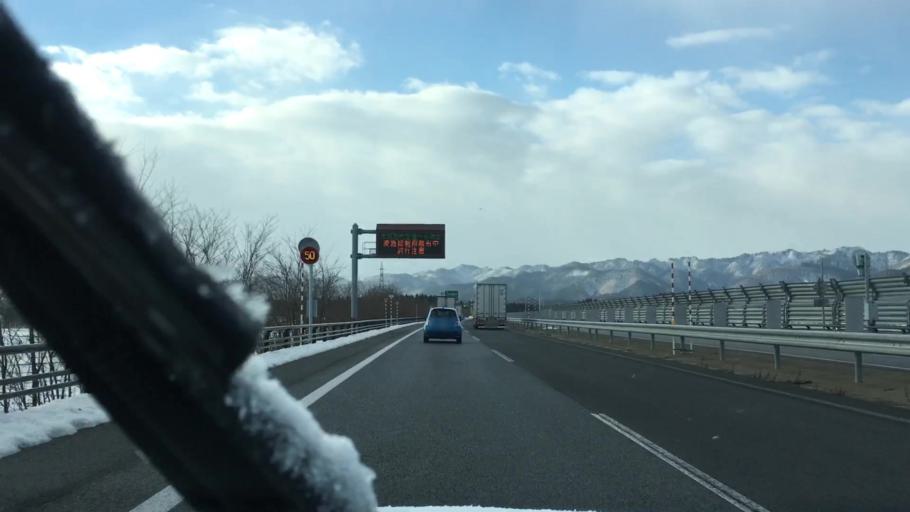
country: JP
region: Akita
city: Odate
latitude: 40.2554
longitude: 140.5201
